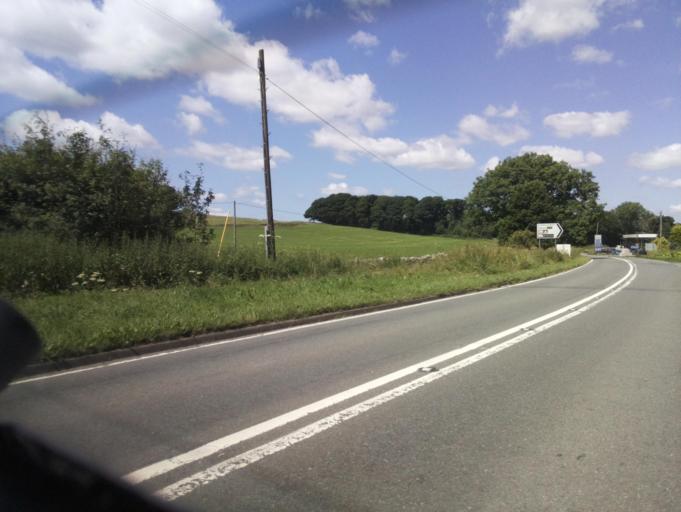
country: GB
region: England
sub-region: Derbyshire
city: Bakewell
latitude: 53.1383
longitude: -1.7529
